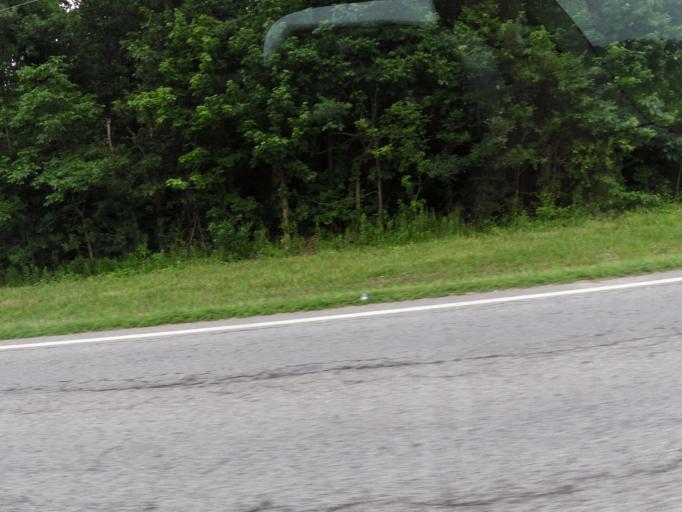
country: US
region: Ohio
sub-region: Brown County
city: Mount Orab
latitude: 39.0893
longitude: -83.9293
